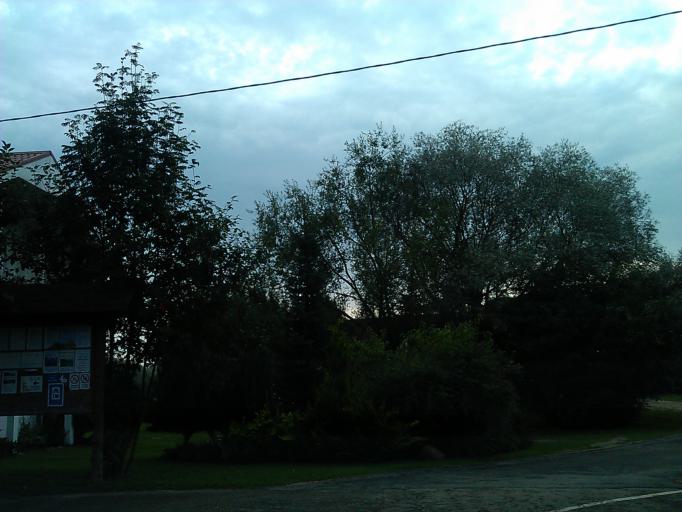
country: LV
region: Lecava
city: Iecava
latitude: 56.5640
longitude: 24.1677
